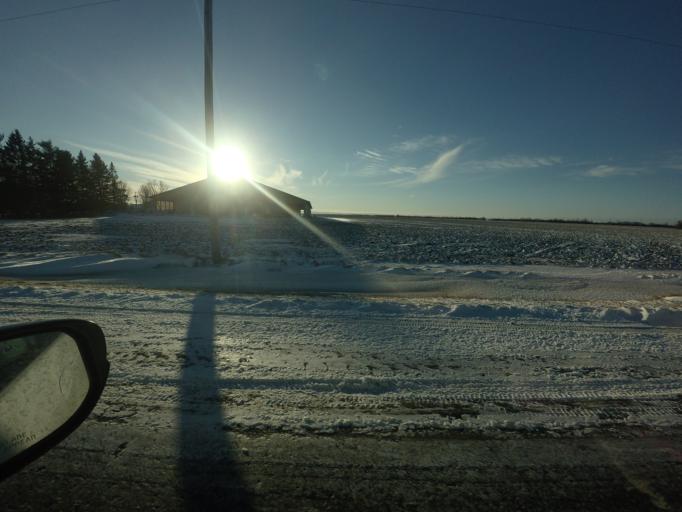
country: CA
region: Ontario
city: Bells Corners
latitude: 45.2546
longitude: -75.8226
